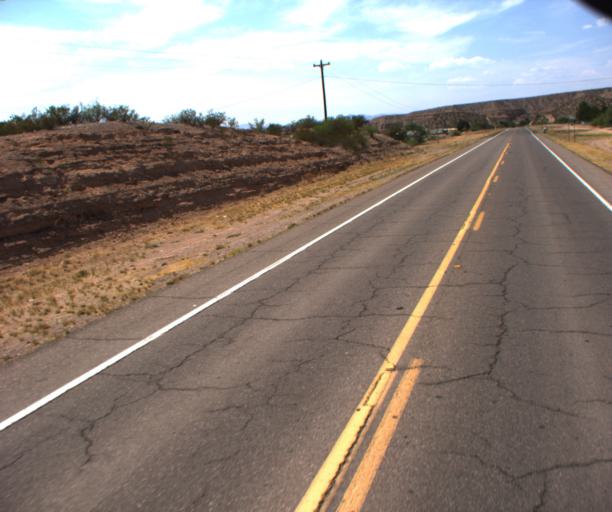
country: US
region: Arizona
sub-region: Greenlee County
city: Clifton
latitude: 32.9194
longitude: -109.1983
